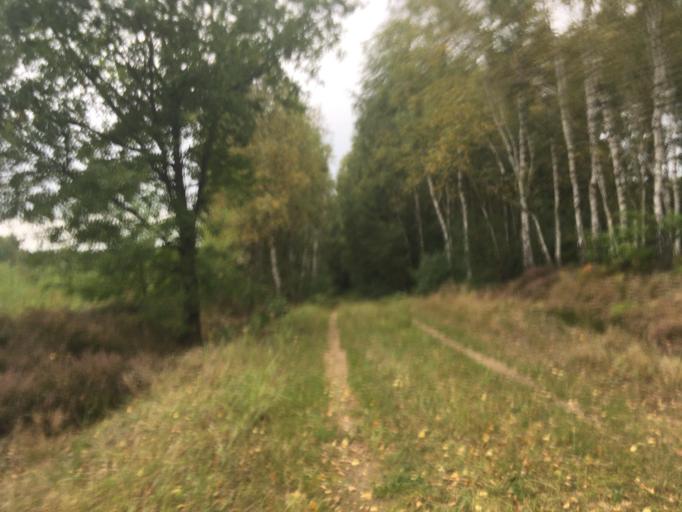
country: DE
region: Brandenburg
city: Glienicke
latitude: 52.6996
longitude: 13.3543
